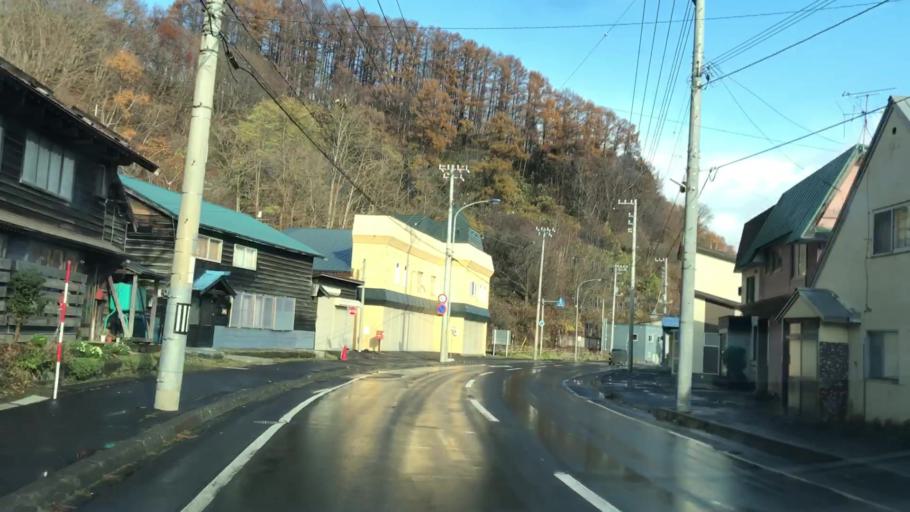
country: JP
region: Hokkaido
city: Yoichi
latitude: 43.2742
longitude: 140.6354
